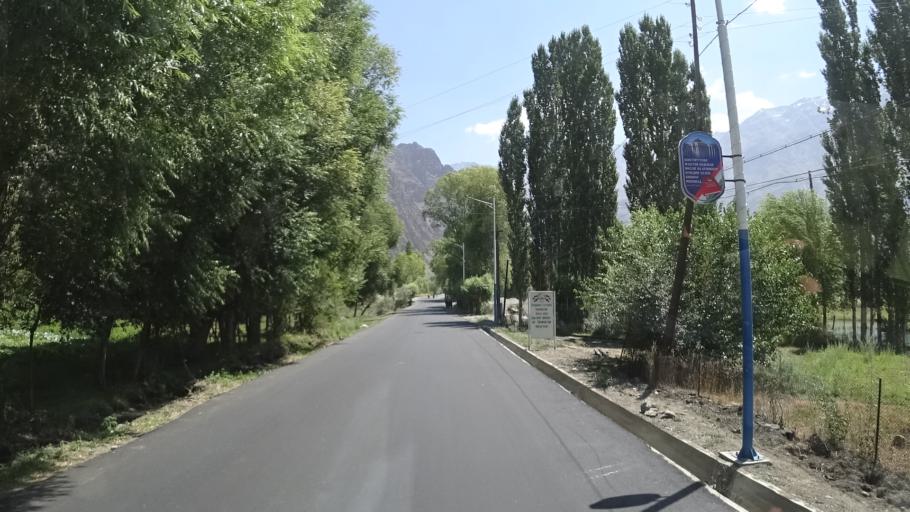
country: TJ
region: Gorno-Badakhshan
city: Rushon
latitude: 37.9465
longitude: 71.5672
